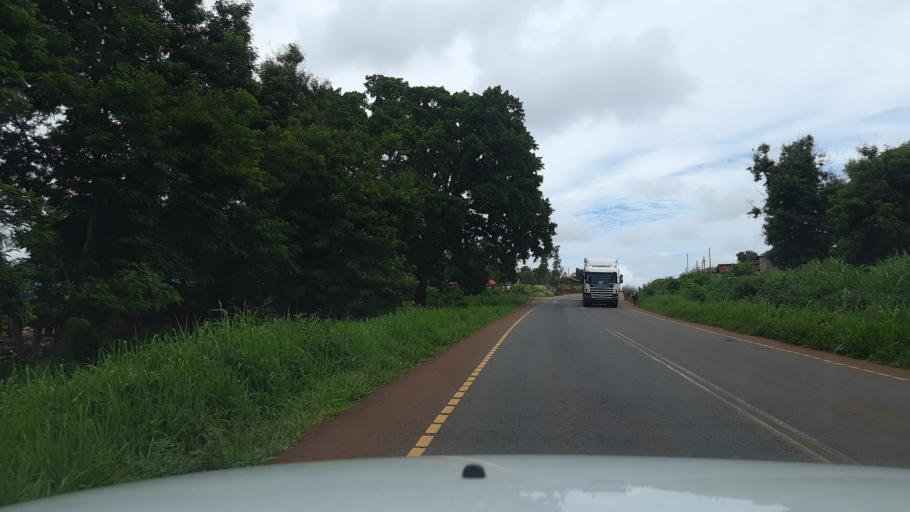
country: TZ
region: Pwani
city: Lugoba
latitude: -6.0841
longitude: 38.2438
